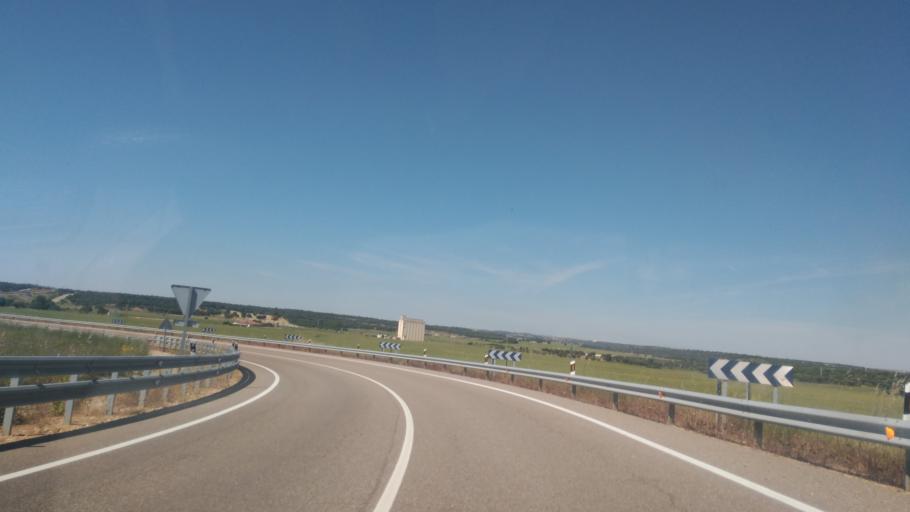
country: ES
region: Castille and Leon
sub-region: Provincia de Salamanca
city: Calzada de Valdunciel
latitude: 41.1229
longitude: -5.6965
